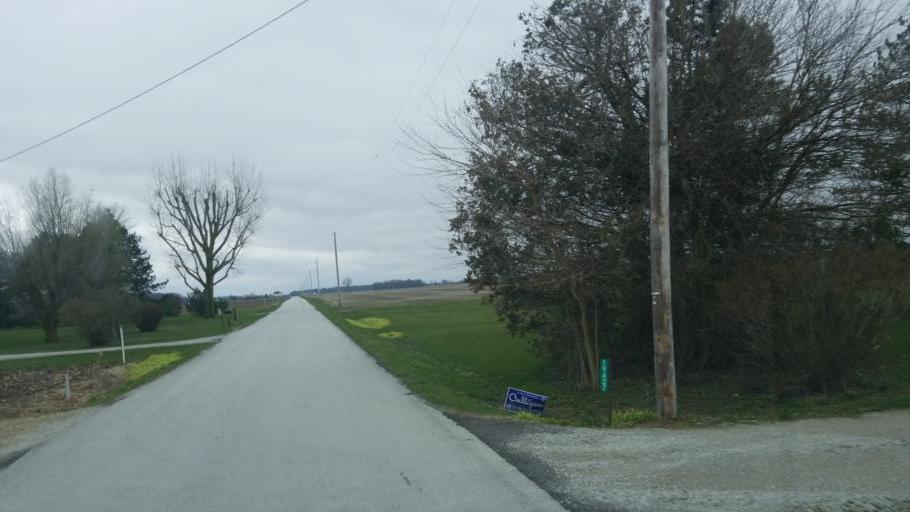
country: US
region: Ohio
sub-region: Hardin County
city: Forest
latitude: 40.7236
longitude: -83.5062
